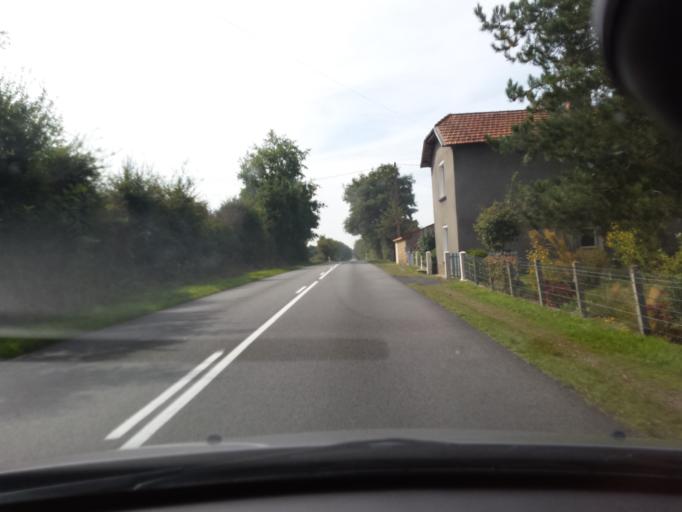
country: FR
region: Pays de la Loire
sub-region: Departement de la Vendee
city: Nieul-le-Dolent
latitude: 46.5836
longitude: -1.4850
